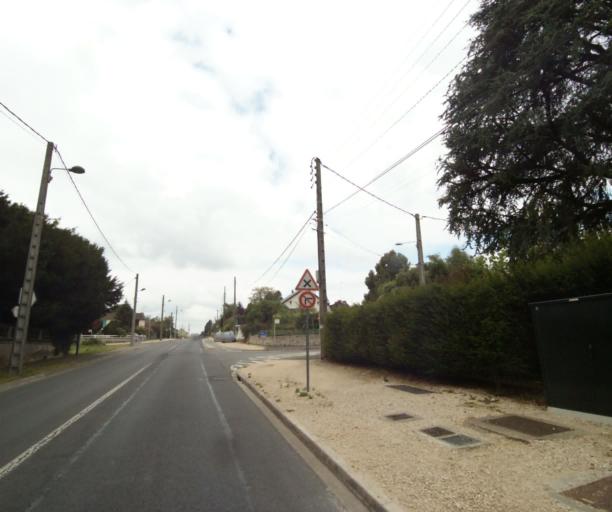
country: FR
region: Centre
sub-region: Departement du Loiret
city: Saint-Jean-de-Braye
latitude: 47.9060
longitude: 1.9869
